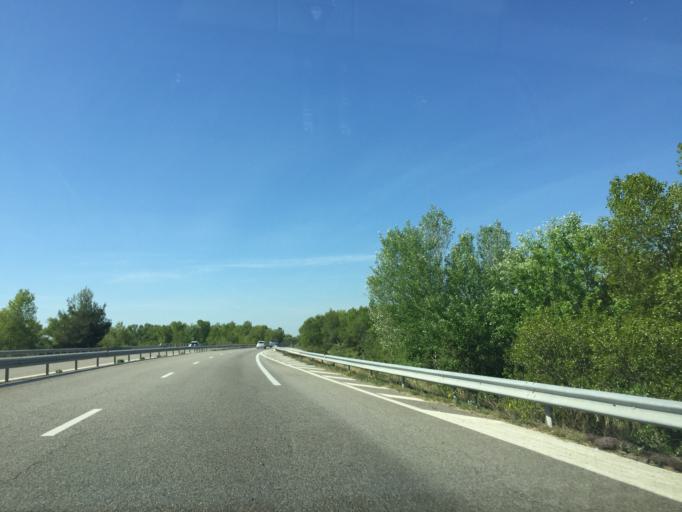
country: FR
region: Provence-Alpes-Cote d'Azur
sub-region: Departement des Alpes-de-Haute-Provence
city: Volx
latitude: 43.8529
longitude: 5.8593
